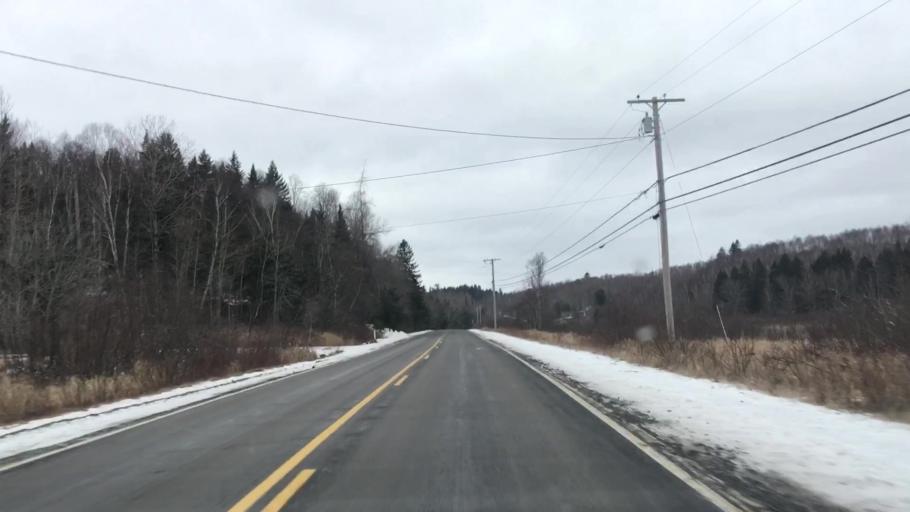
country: US
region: Maine
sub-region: Washington County
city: Machiasport
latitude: 44.7097
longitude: -67.3691
